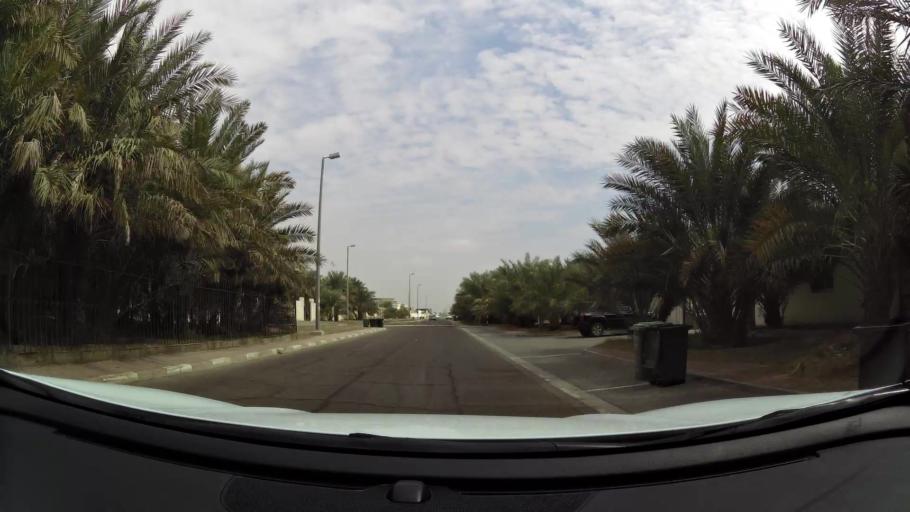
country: AE
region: Abu Dhabi
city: Al Ain
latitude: 24.1994
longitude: 55.7996
